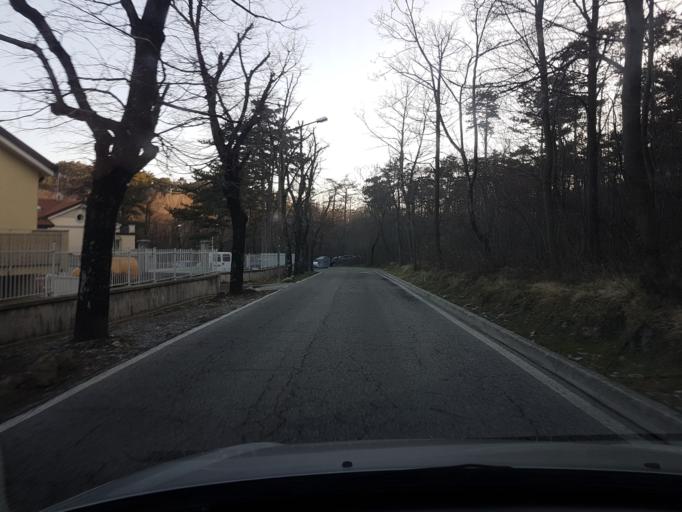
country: IT
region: Friuli Venezia Giulia
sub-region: Provincia di Trieste
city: Villa Opicina
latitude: 45.6830
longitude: 13.7820
